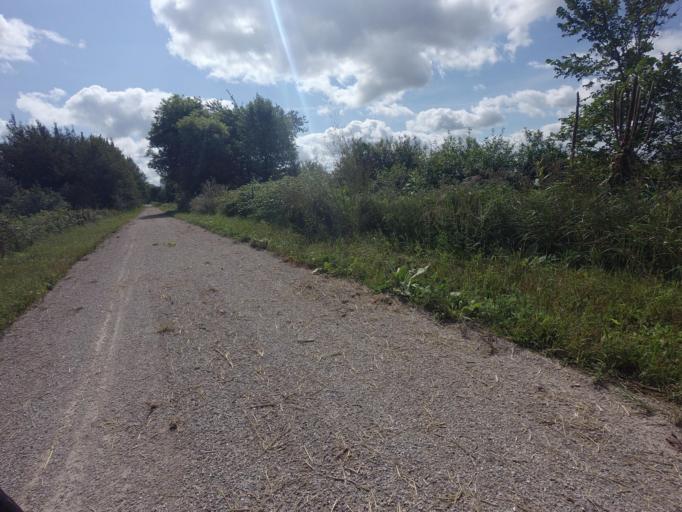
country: CA
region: Ontario
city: Huron East
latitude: 43.6502
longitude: -81.2267
